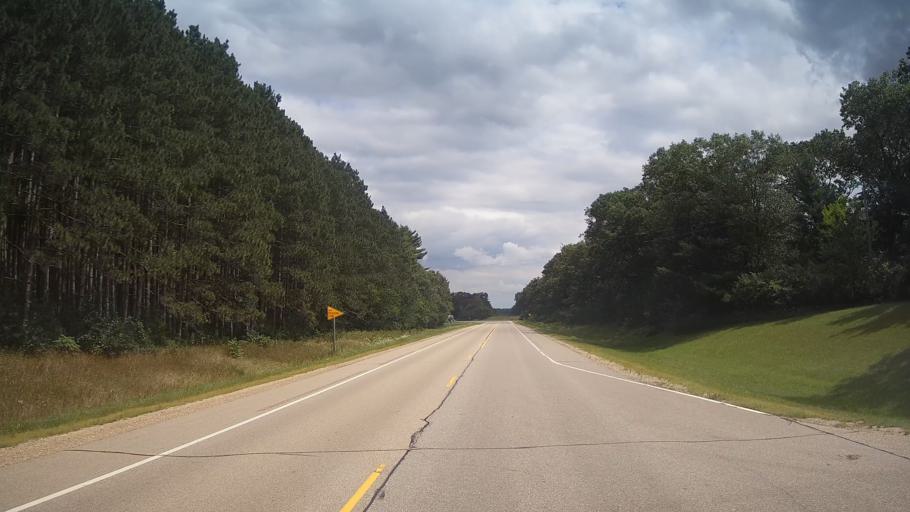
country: US
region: Wisconsin
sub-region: Marquette County
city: Westfield
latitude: 44.0218
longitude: -89.5510
